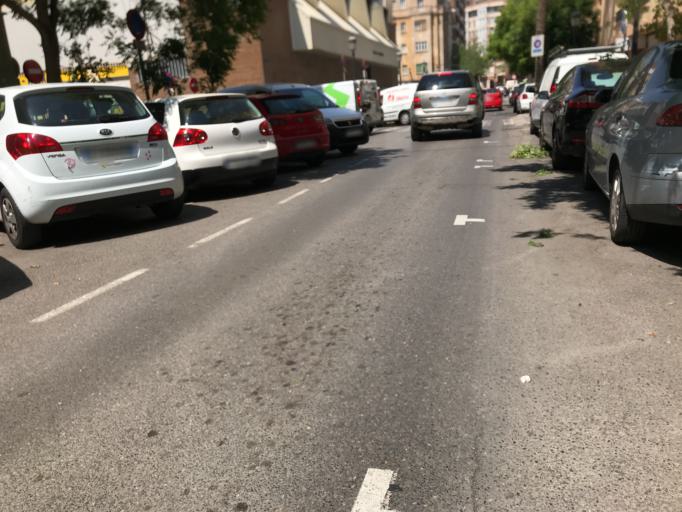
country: ES
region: Valencia
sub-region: Provincia de Valencia
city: Valencia
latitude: 39.4699
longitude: -0.3526
